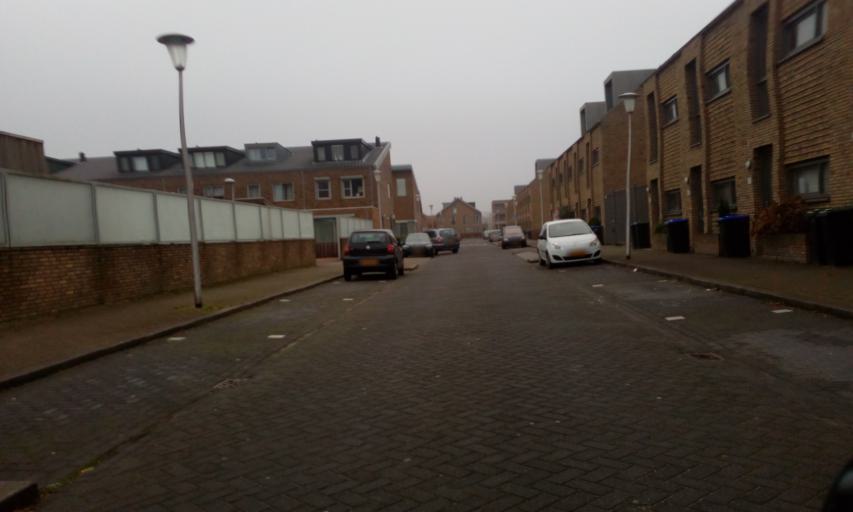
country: NL
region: South Holland
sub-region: Gemeente Lansingerland
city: Berkel en Rodenrijs
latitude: 51.9989
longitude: 4.4653
